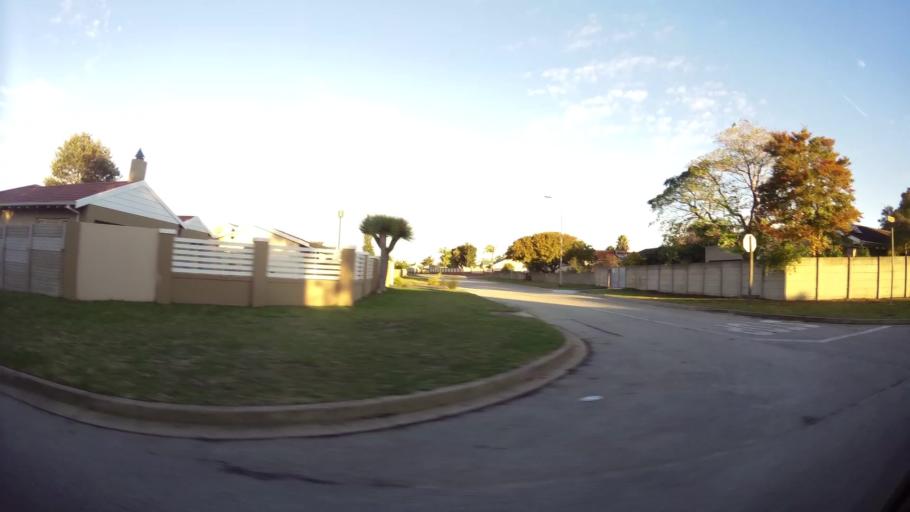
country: ZA
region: Eastern Cape
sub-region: Nelson Mandela Bay Metropolitan Municipality
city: Port Elizabeth
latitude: -33.9722
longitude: 25.5196
